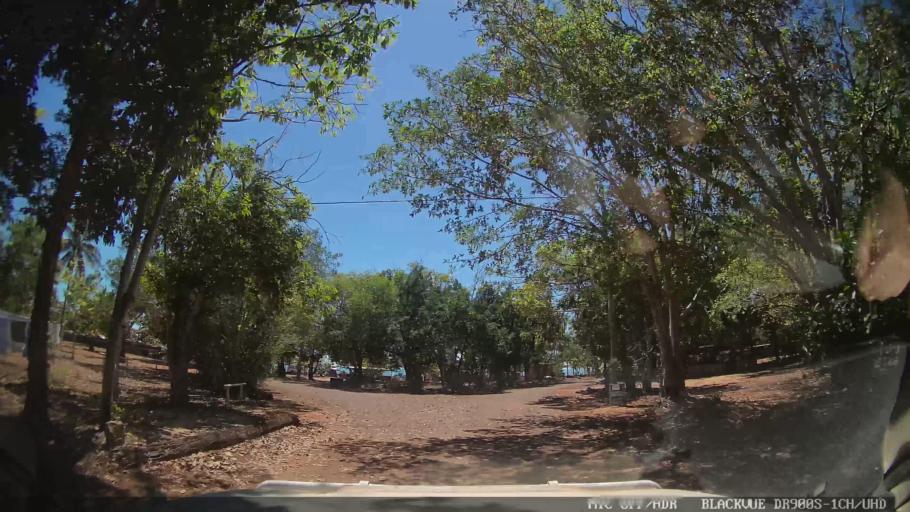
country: AU
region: Queensland
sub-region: Torres
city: Thursday Island
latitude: -10.8469
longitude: 142.3682
